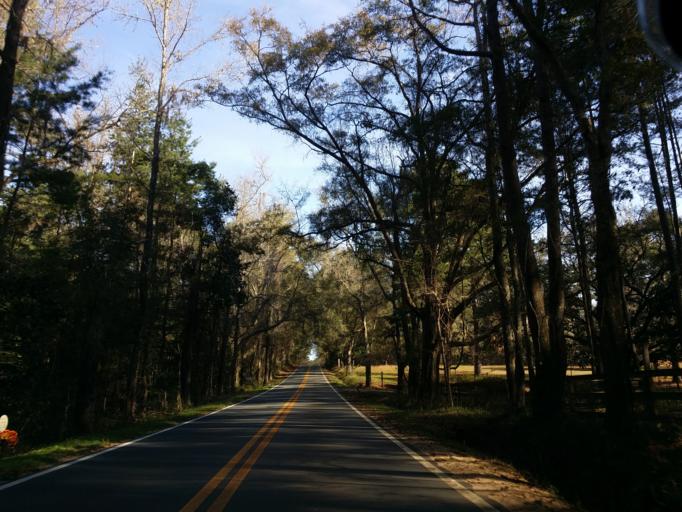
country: US
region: Florida
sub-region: Leon County
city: Woodville
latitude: 30.3882
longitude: -84.1553
